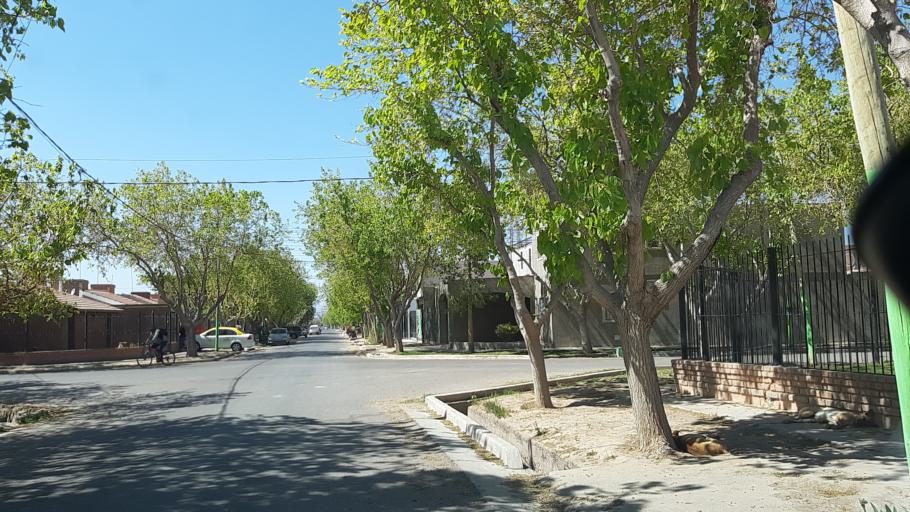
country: AR
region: San Juan
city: San Juan
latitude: -31.5216
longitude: -68.5889
